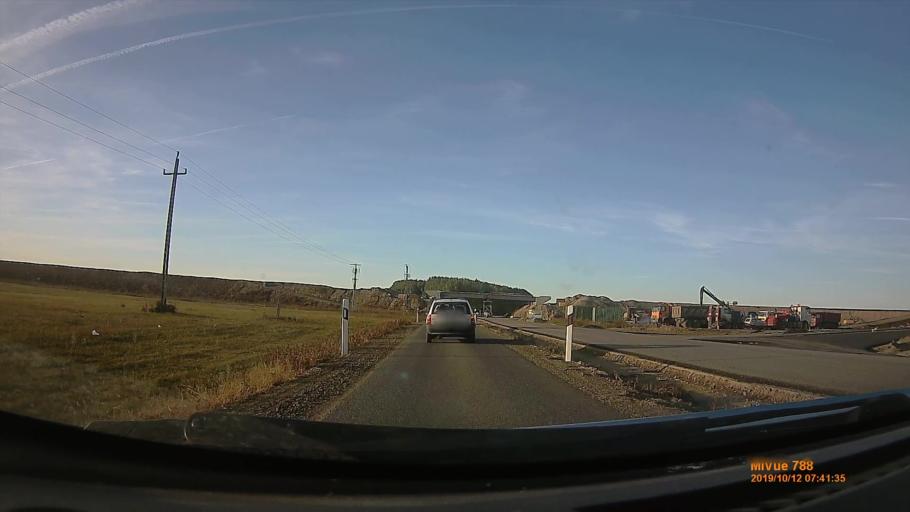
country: HU
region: Hajdu-Bihar
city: Pocsaj
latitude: 47.2055
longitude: 21.7966
